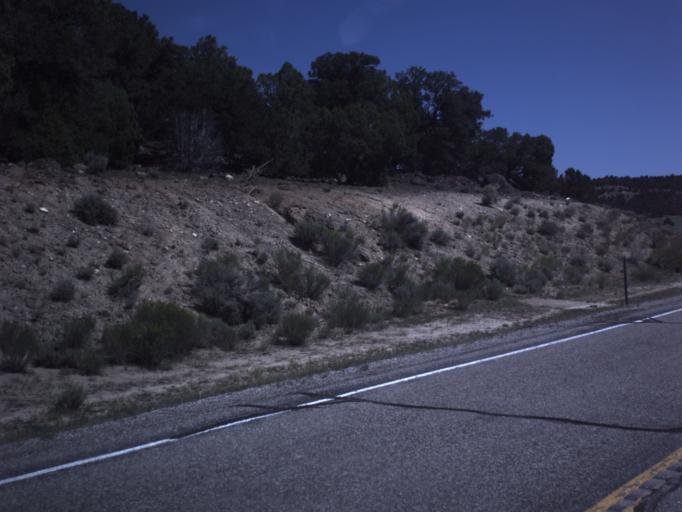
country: US
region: Utah
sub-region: Wayne County
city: Loa
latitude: 38.6815
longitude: -111.3987
